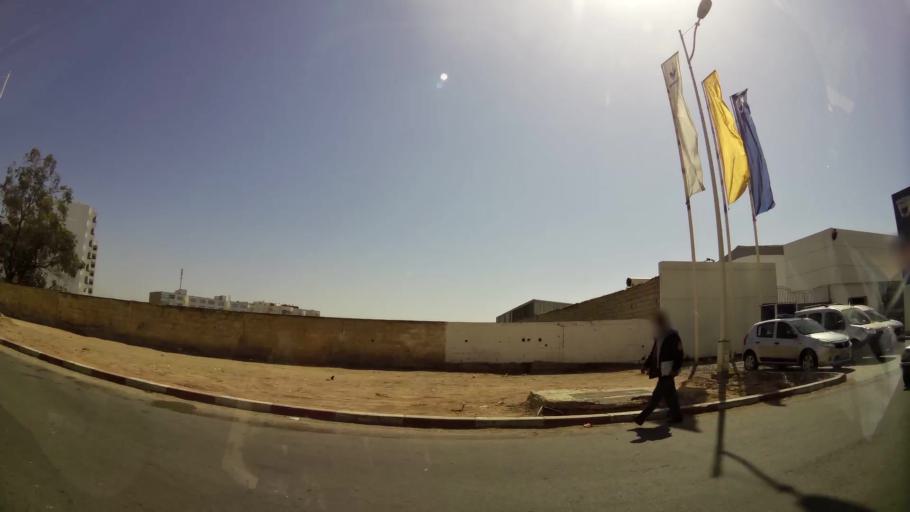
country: MA
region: Souss-Massa-Draa
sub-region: Agadir-Ida-ou-Tnan
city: Agadir
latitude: 30.4191
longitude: -9.5783
